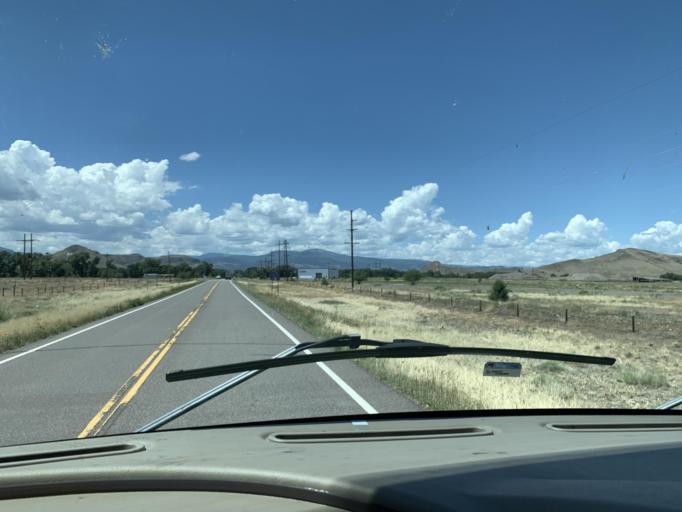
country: US
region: Colorado
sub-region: Rio Grande County
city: Del Norte
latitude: 37.6951
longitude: -106.3381
